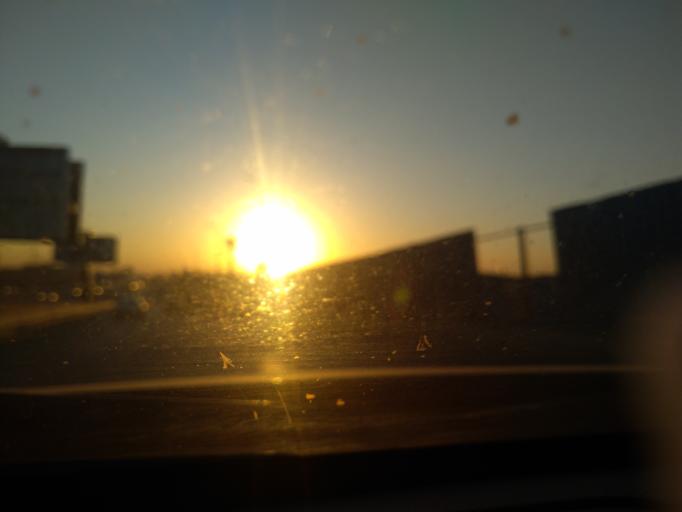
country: EG
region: Muhafazat al Qalyubiyah
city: Al Khankah
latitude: 30.0835
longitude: 31.4695
